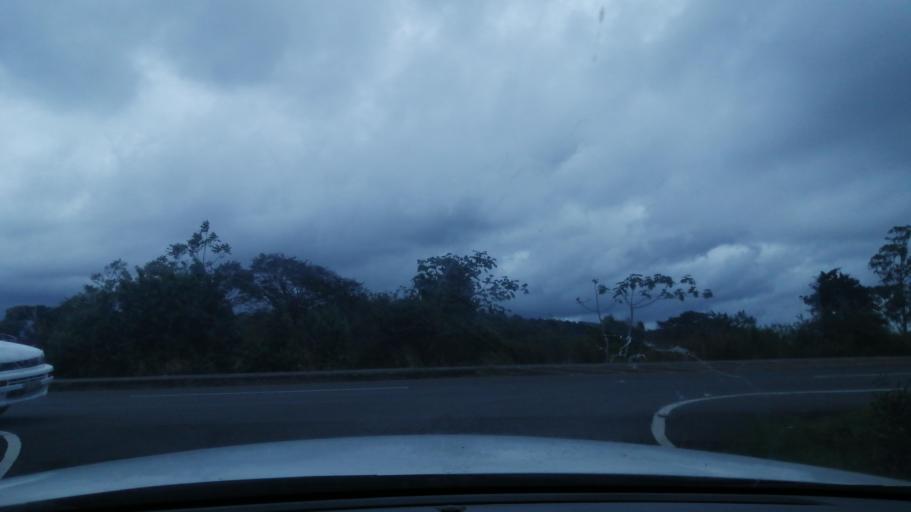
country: PA
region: Chiriqui
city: Palmira
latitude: 8.6872
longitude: -82.4514
